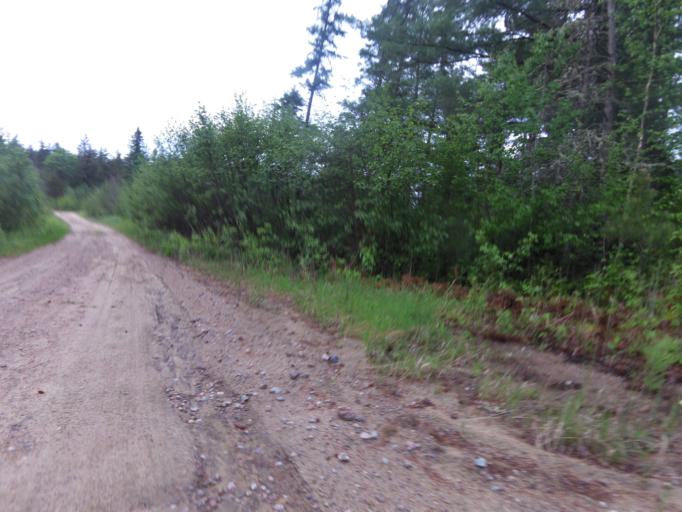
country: CA
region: Quebec
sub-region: Outaouais
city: Shawville
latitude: 45.9106
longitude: -76.2984
